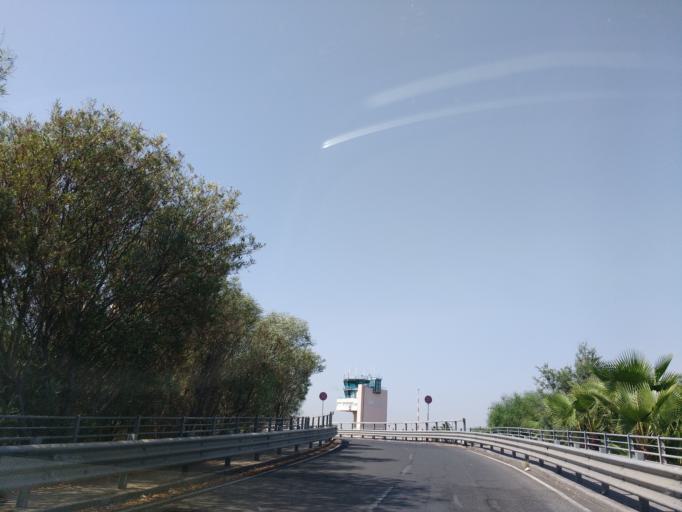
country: IT
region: Sicily
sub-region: Catania
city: Catania
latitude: 37.4717
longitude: 15.0654
